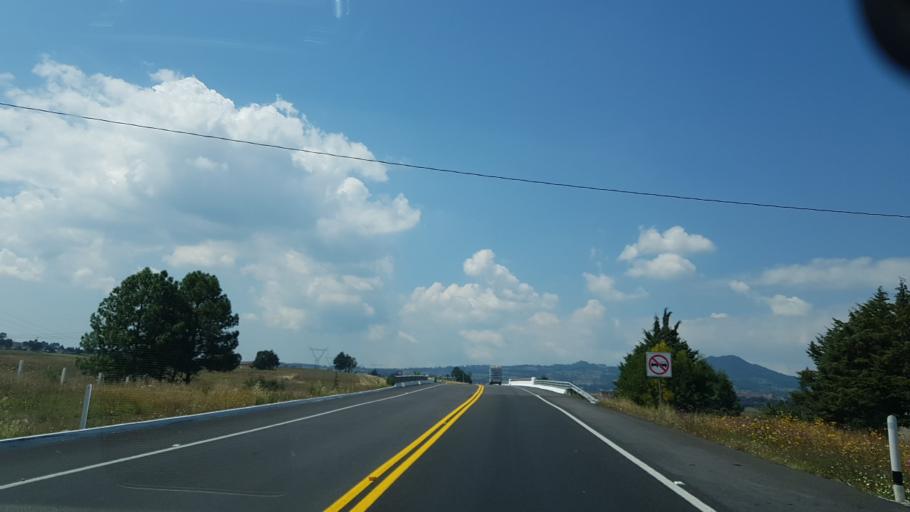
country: MX
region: Mexico
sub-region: Villa Victoria
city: Colonia Doctor Gustavo Baz
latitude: 19.3728
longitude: -99.9255
